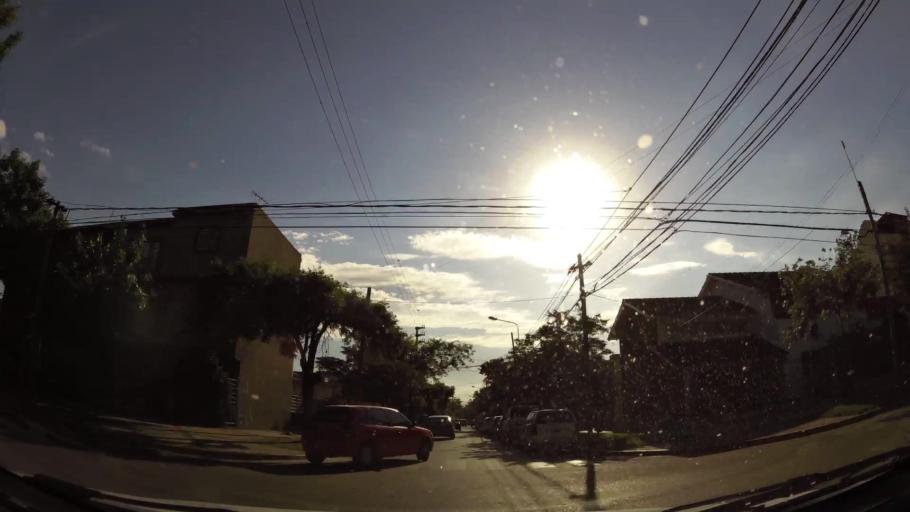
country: AR
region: Buenos Aires
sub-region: Partido de Merlo
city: Merlo
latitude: -34.6707
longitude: -58.7274
